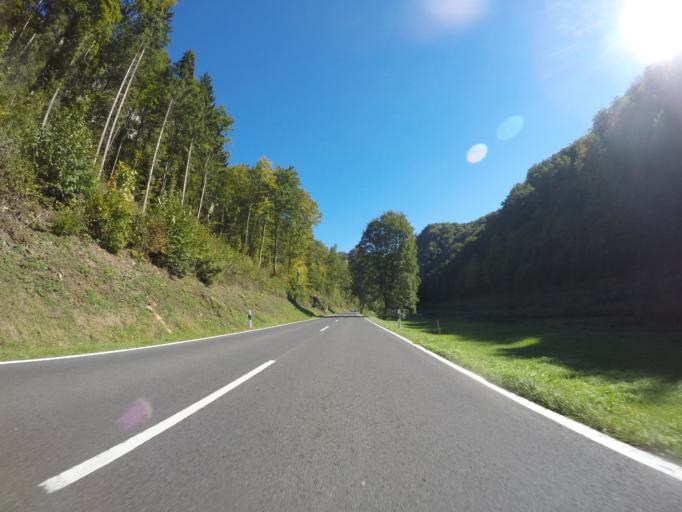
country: DE
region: Bavaria
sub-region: Upper Franconia
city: Gossweinstein
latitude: 49.7714
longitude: 11.3234
